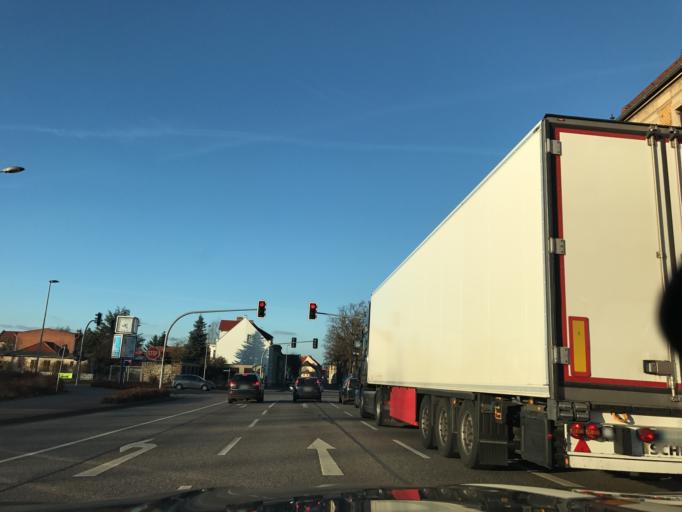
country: DE
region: Saxony-Anhalt
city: Burg bei Magdeburg
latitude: 52.2652
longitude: 11.8619
